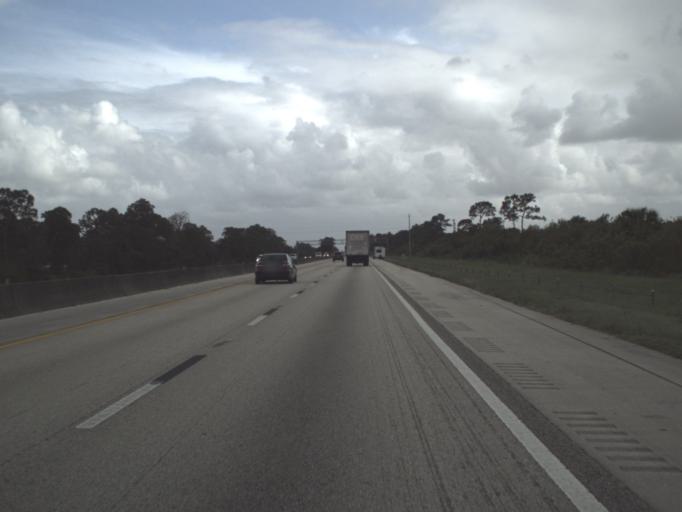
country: US
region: Florida
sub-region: Palm Beach County
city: Limestone Creek
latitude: 26.9774
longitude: -80.1825
